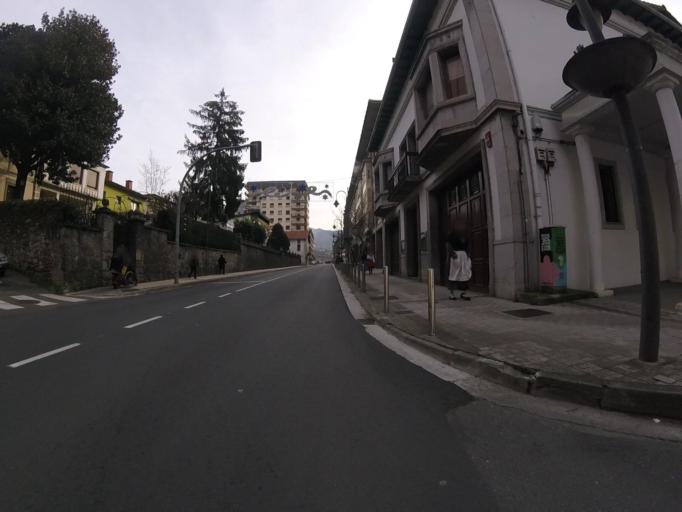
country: ES
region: Basque Country
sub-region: Provincia de Guipuzcoa
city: Ibarra
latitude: 43.1331
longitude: -2.0689
